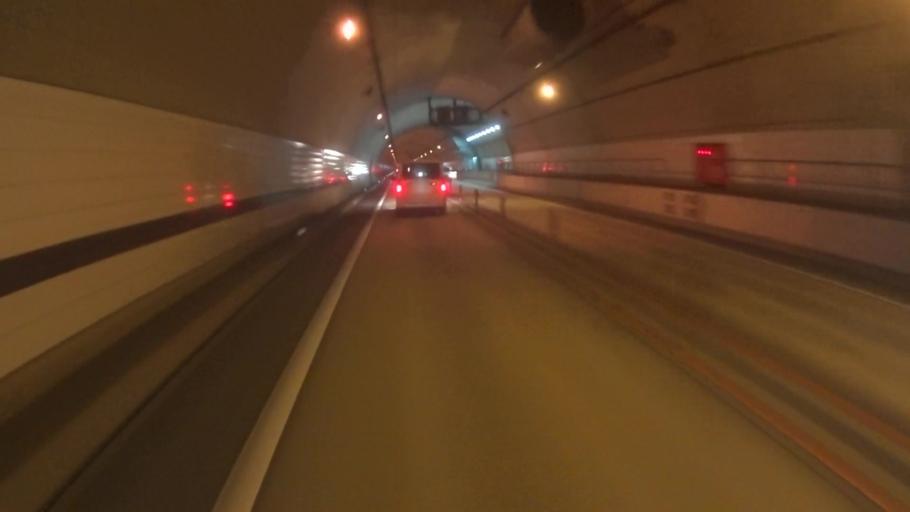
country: JP
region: Kyoto
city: Miyazu
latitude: 35.4844
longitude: 135.1739
